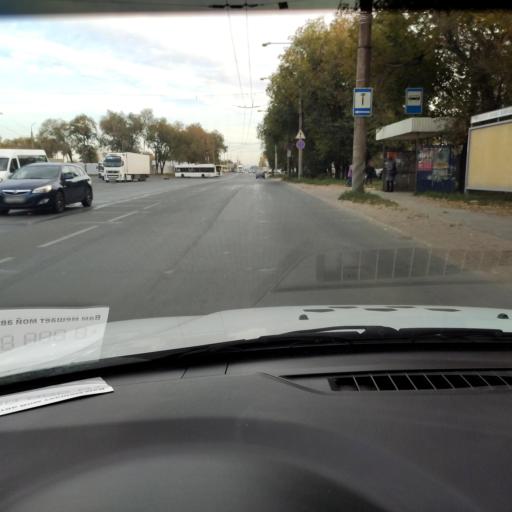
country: RU
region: Samara
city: Tol'yatti
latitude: 53.5673
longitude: 49.4576
